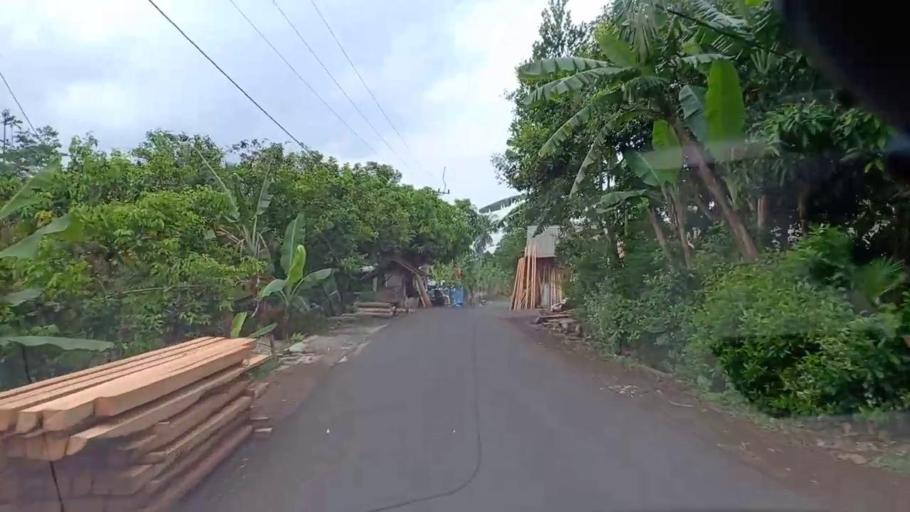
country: ID
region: West Java
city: Gerempay
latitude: -7.3370
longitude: 108.2931
